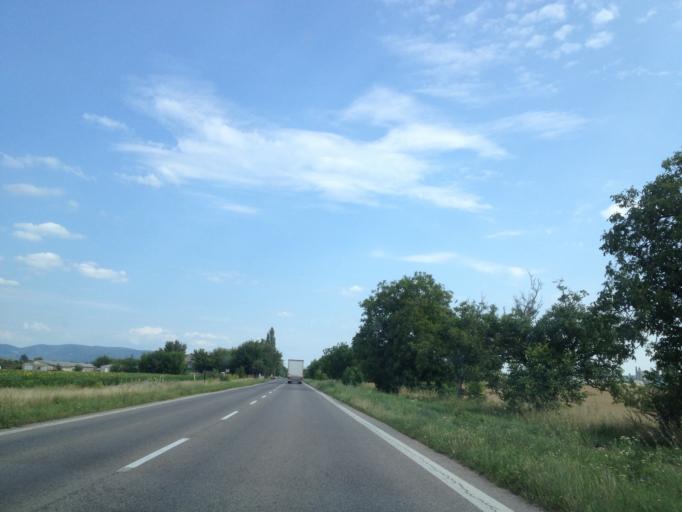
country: SK
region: Nitriansky
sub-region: Okres Nove Zamky
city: Sturovo
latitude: 47.7958
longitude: 18.6931
